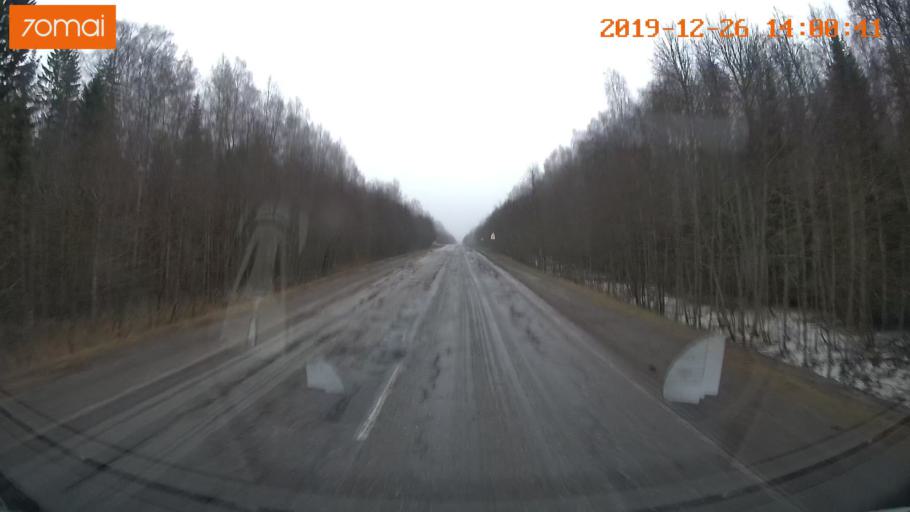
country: RU
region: Jaroslavl
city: Poshekhon'ye
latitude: 58.5563
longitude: 38.7482
